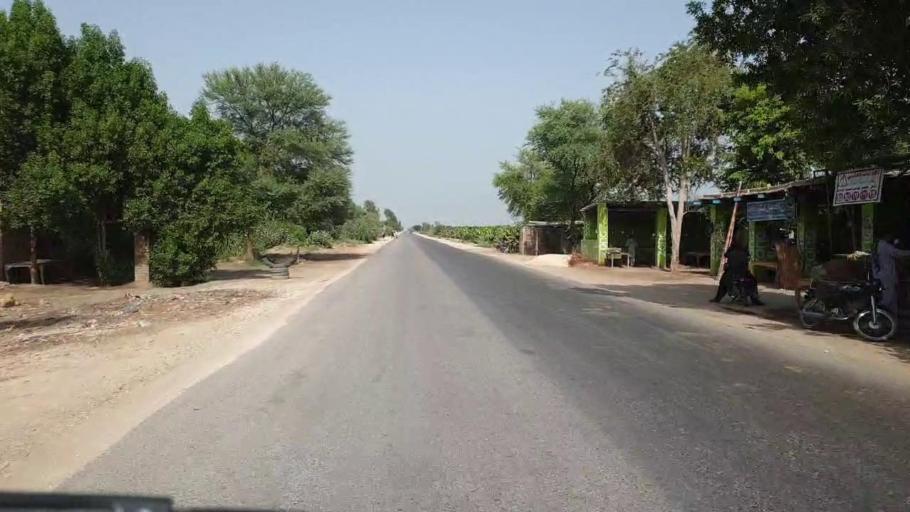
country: PK
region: Sindh
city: Sakrand
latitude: 26.2451
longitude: 68.2416
